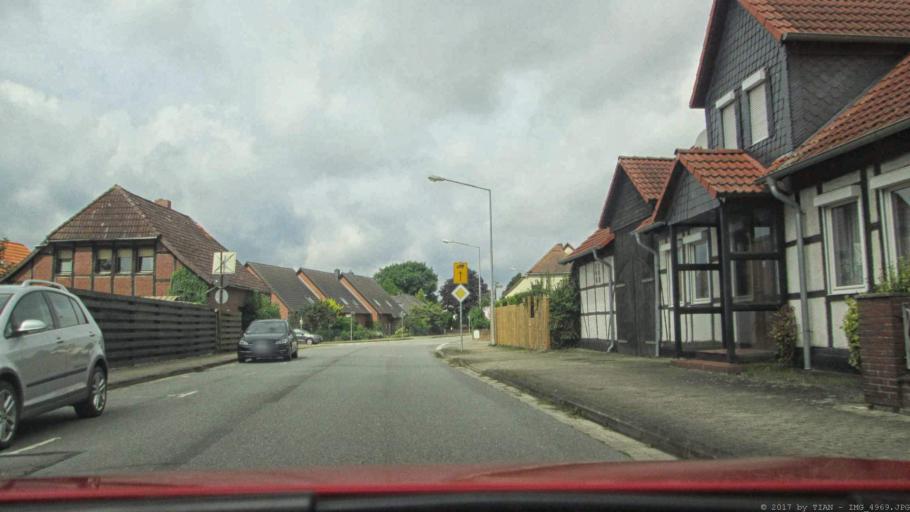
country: DE
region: Lower Saxony
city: Tappenbeck
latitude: 52.4570
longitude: 10.7476
